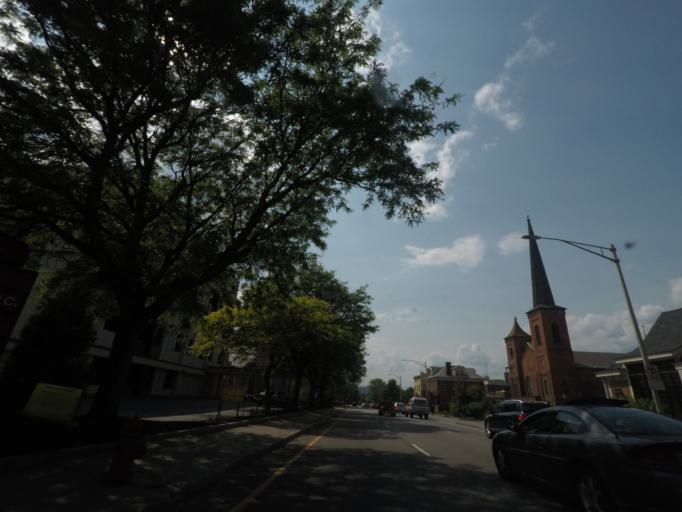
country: US
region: New York
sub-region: Dutchess County
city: Poughkeepsie
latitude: 41.7050
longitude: -73.9264
